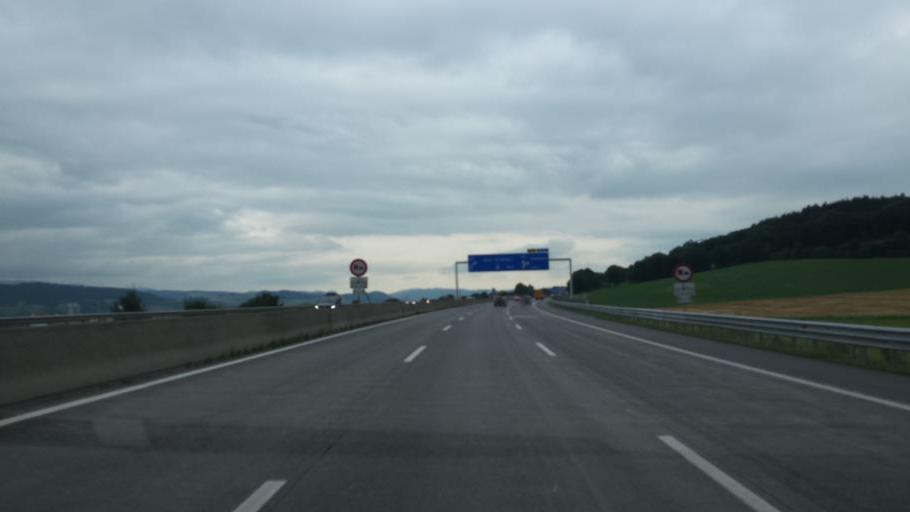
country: AT
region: Lower Austria
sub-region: Politischer Bezirk Melk
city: Pochlarn
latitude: 48.1906
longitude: 15.2002
